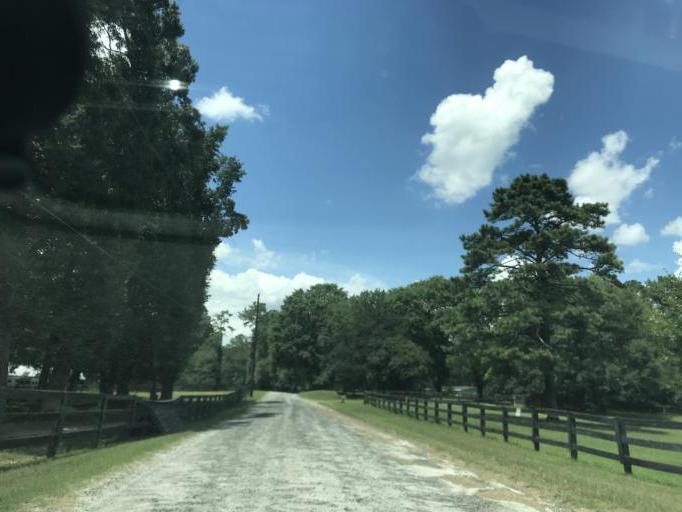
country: US
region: Georgia
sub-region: Gwinnett County
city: Suwanee
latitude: 34.0583
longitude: -84.1187
